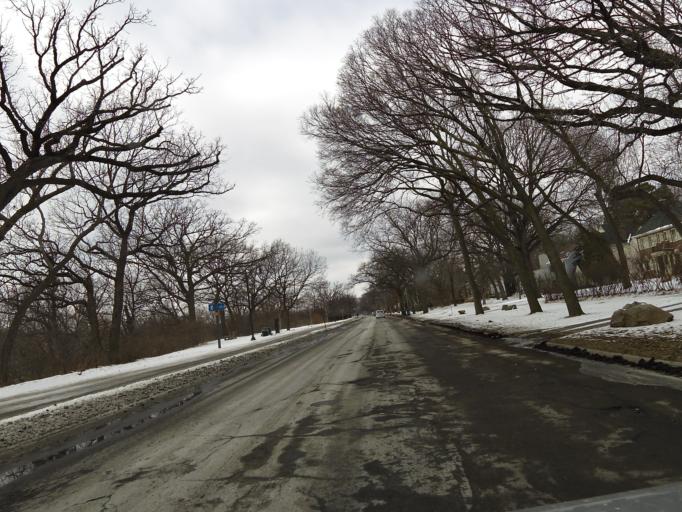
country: US
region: Minnesota
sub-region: Ramsey County
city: Lauderdale
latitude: 44.9600
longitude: -93.2141
